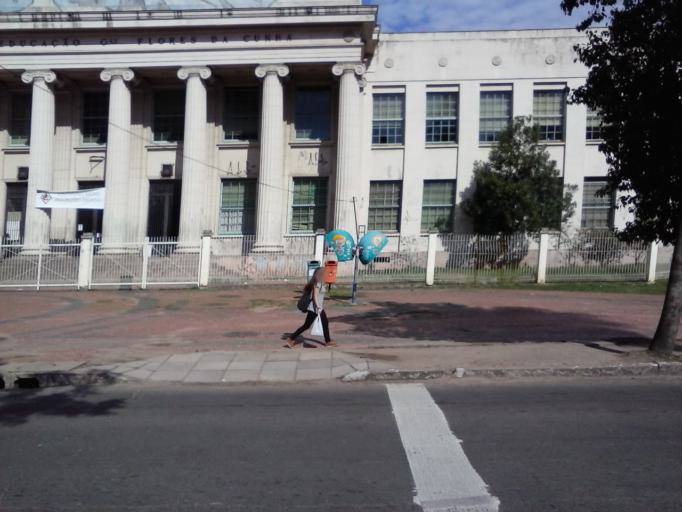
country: BR
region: Rio Grande do Sul
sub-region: Porto Alegre
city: Porto Alegre
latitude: -30.0330
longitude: -51.2173
